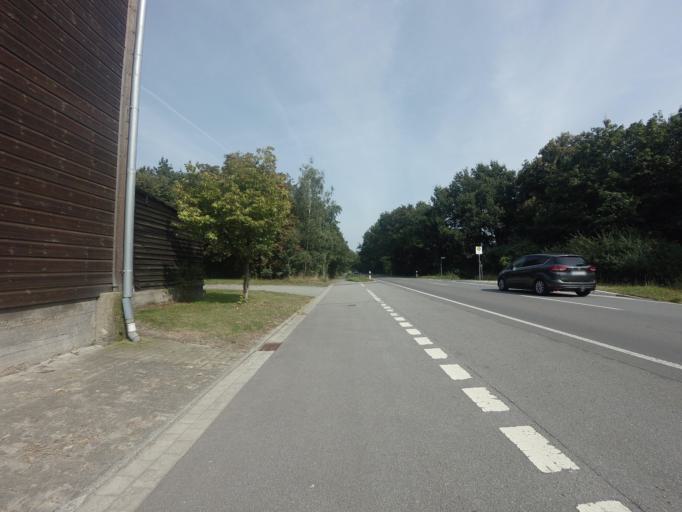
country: DE
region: Lower Saxony
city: Wielen
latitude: 52.5328
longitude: 6.7372
